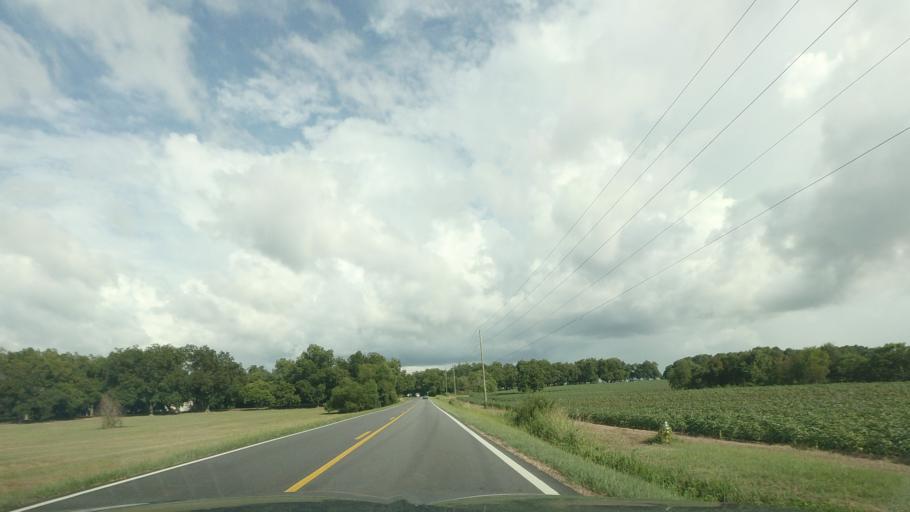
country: US
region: Georgia
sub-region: Peach County
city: Byron
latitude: 32.6360
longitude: -83.7311
